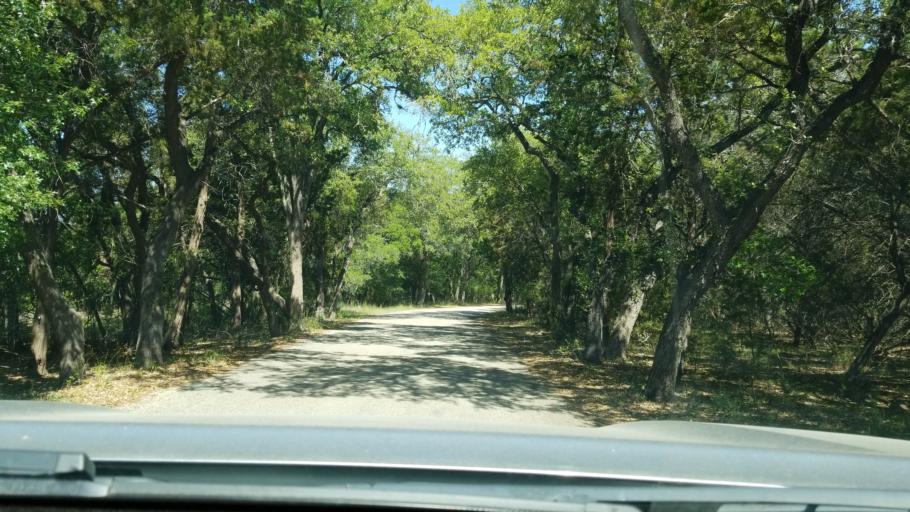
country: US
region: Texas
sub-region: Bexar County
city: Timberwood Park
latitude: 29.7501
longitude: -98.5174
